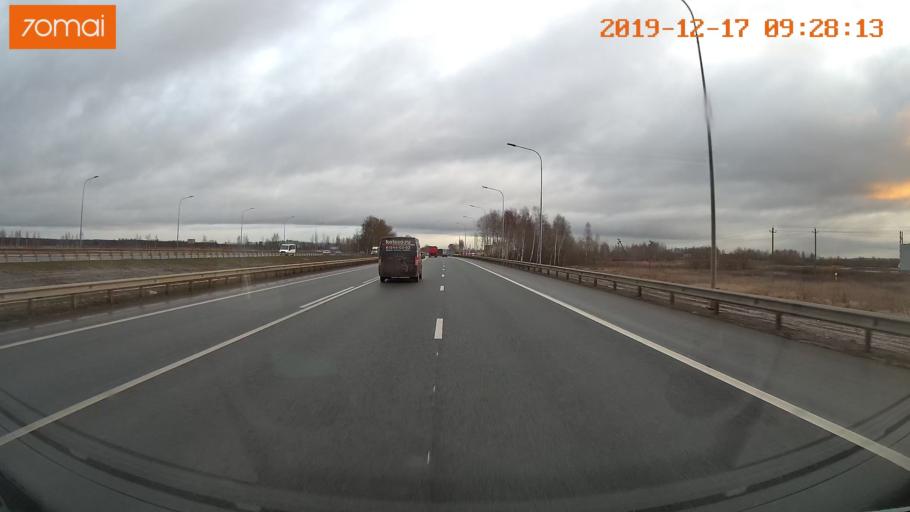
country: RU
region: Vladimir
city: Vorsha
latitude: 56.0557
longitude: 40.1068
